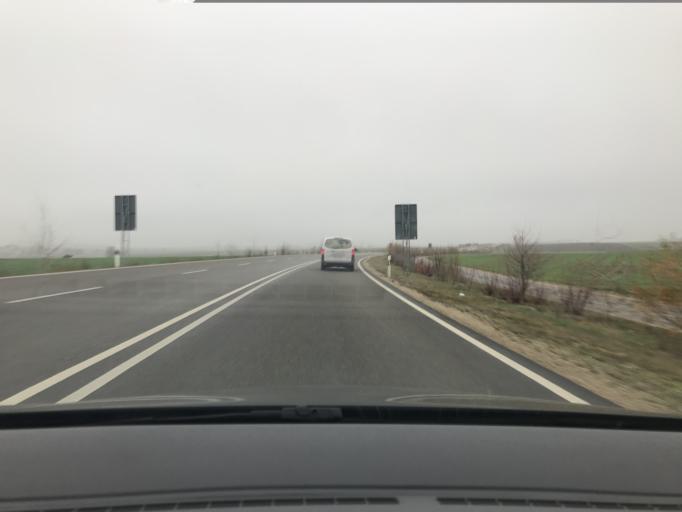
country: DE
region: Bavaria
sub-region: Swabia
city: Wallerstein
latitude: 48.8759
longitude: 10.4535
